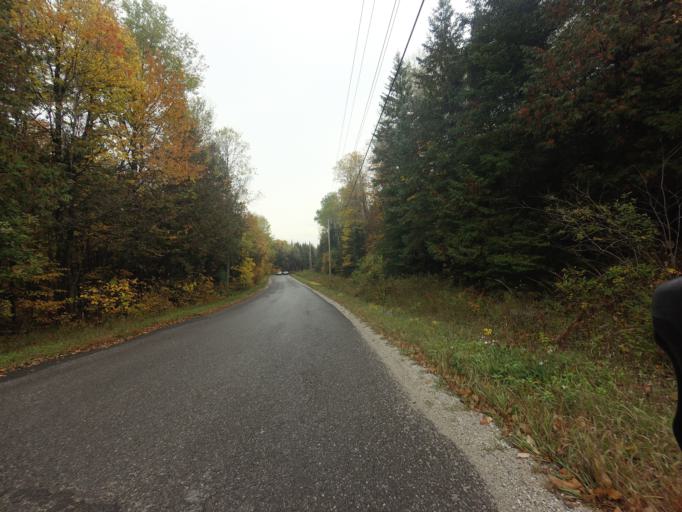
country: CA
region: Ontario
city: Perth
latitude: 45.1153
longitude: -76.5083
